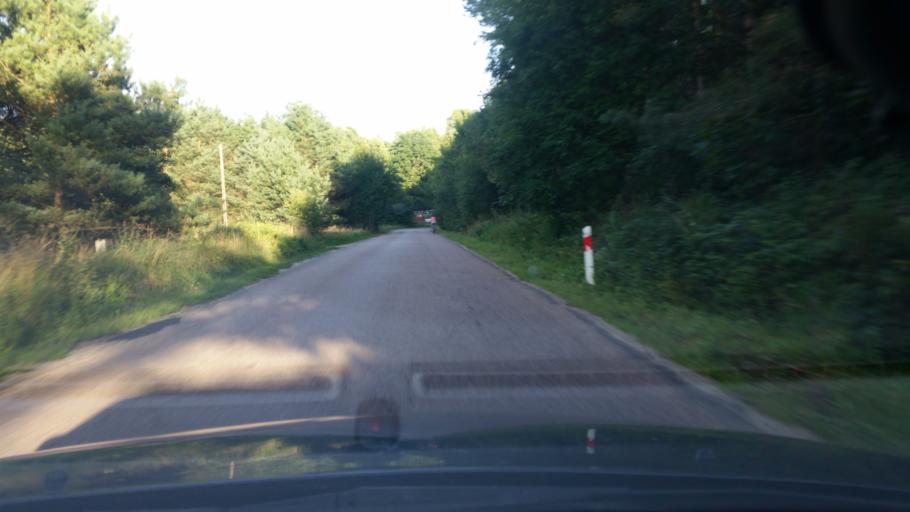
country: PL
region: Pomeranian Voivodeship
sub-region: Powiat wejherowski
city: Choczewo
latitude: 54.7626
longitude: 17.7691
